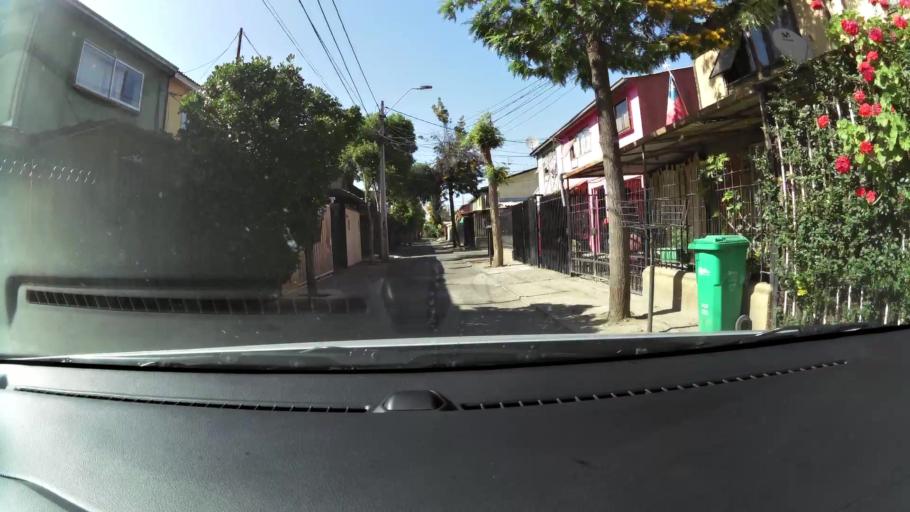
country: CL
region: Santiago Metropolitan
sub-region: Provincia de Maipo
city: San Bernardo
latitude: -33.5638
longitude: -70.7030
